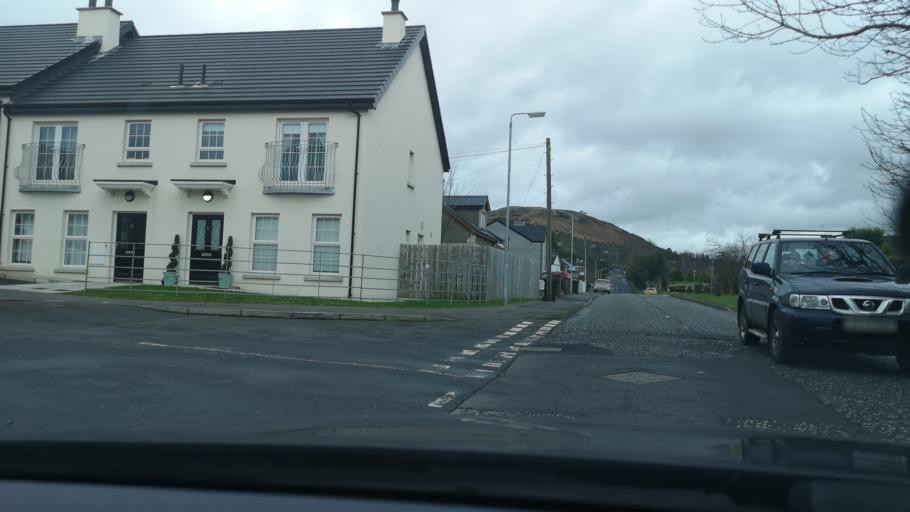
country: GB
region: Northern Ireland
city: Rostrevor
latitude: 54.1083
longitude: -6.1880
